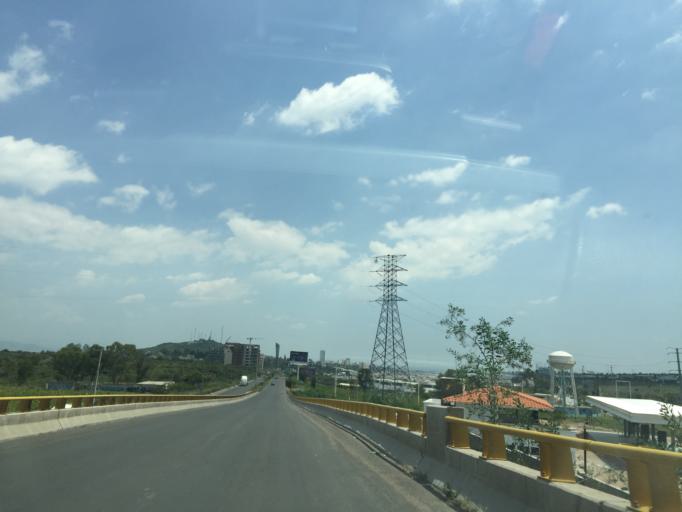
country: MX
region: Guanajuato
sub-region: Leon
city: Fraccionamiento Paseo de las Torres
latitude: 21.1771
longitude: -101.7405
